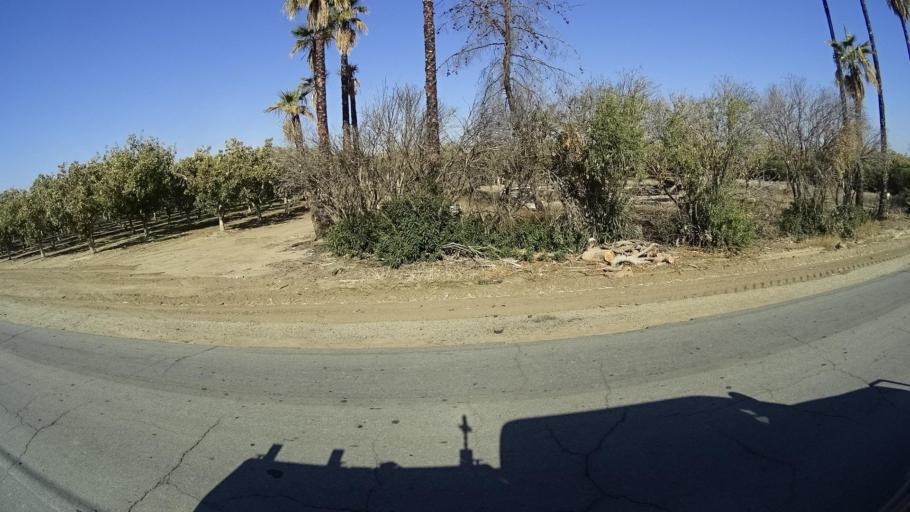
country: US
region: California
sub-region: Kern County
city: McFarland
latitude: 35.7178
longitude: -119.1968
